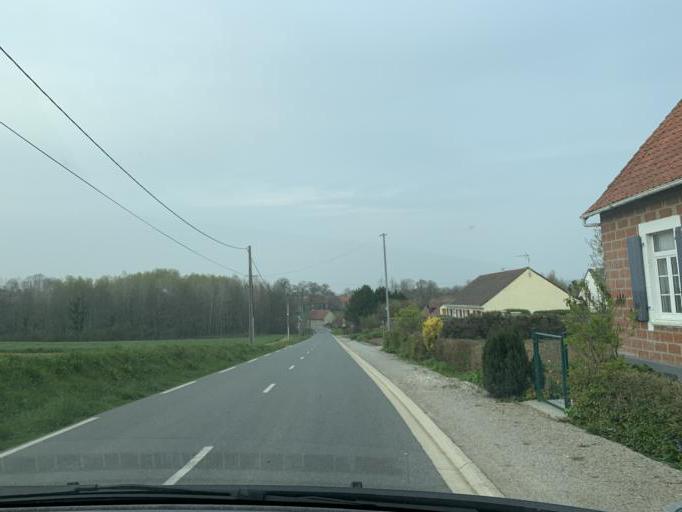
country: FR
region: Nord-Pas-de-Calais
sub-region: Departement du Pas-de-Calais
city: Samer
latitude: 50.6686
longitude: 1.7523
